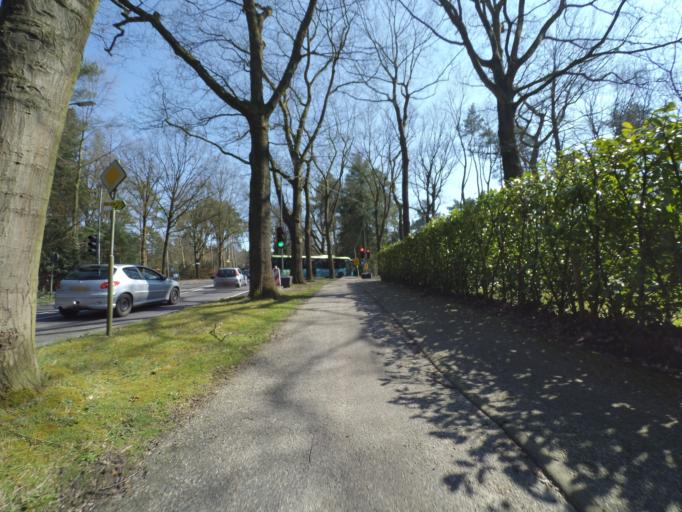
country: NL
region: Utrecht
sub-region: Gemeente Utrechtse Heuvelrug
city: Driebergen-Rijsenburg
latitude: 52.0550
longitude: 5.3021
